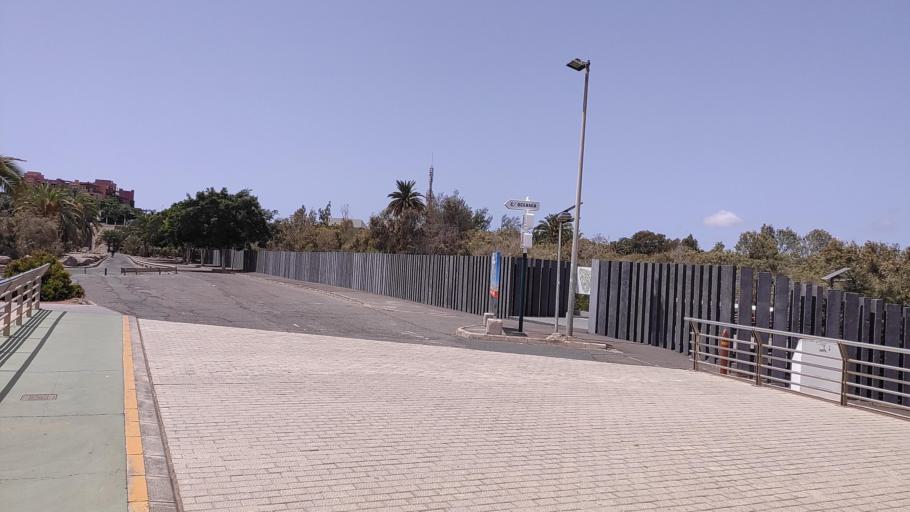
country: ES
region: Canary Islands
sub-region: Provincia de Las Palmas
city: Maspalomas
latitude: 27.7443
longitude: -15.5965
